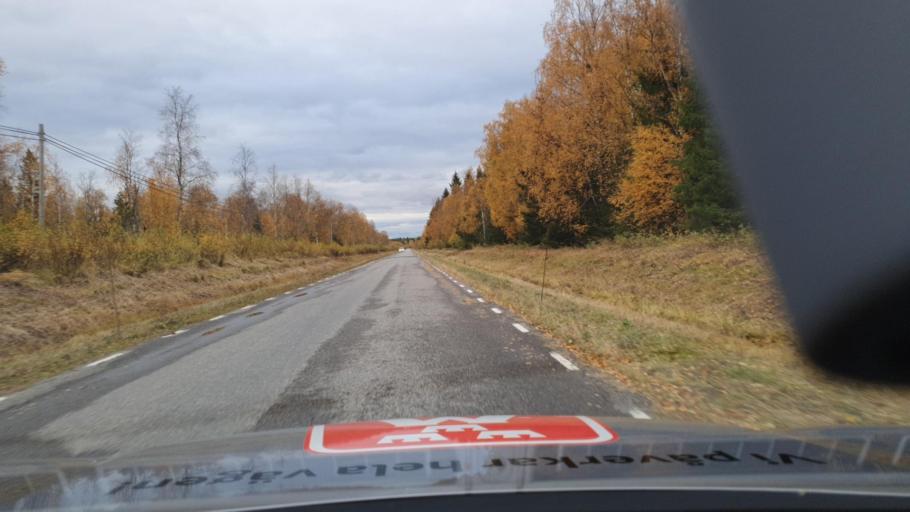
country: FI
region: Lapland
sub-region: Kemi-Tornio
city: Tornio
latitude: 66.0425
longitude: 23.9075
